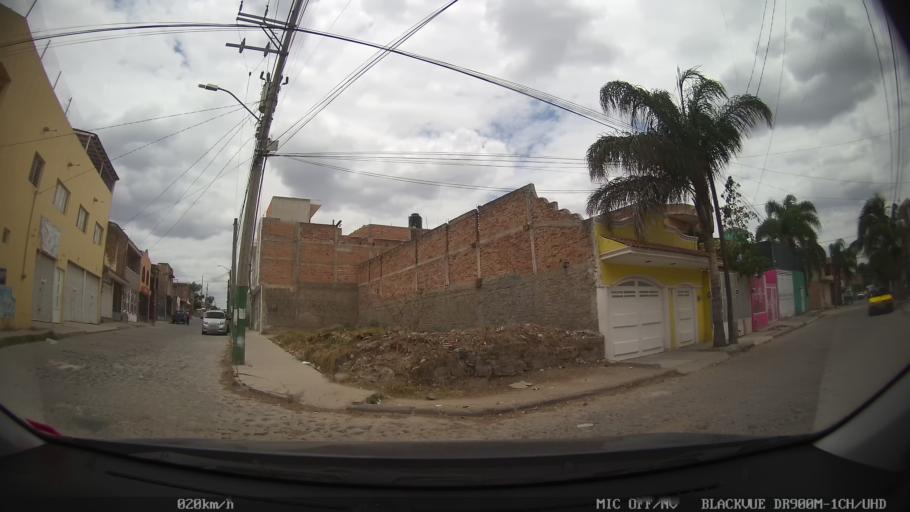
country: MX
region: Jalisco
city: Tlaquepaque
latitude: 20.6479
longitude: -103.2623
